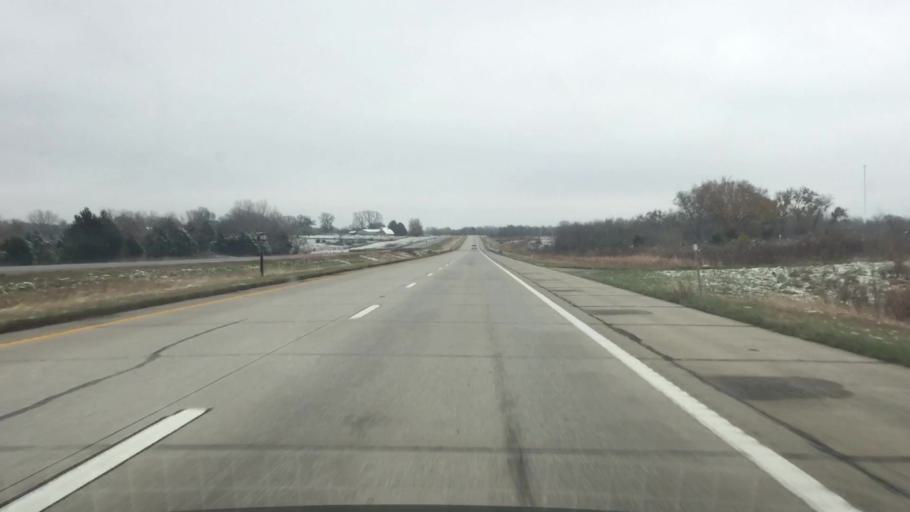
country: US
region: Missouri
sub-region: Saint Clair County
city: Osceola
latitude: 38.1970
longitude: -93.7458
